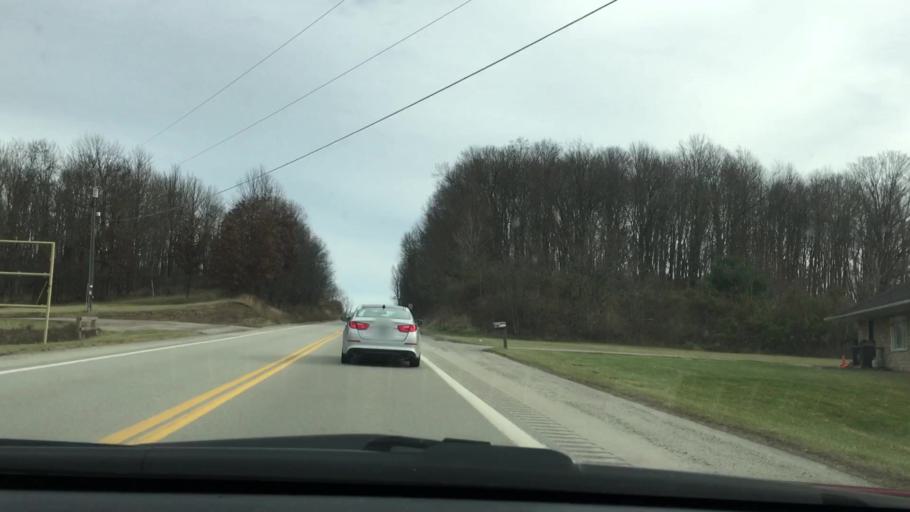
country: US
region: Pennsylvania
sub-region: Fayette County
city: South Uniontown
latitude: 39.8928
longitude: -79.8269
